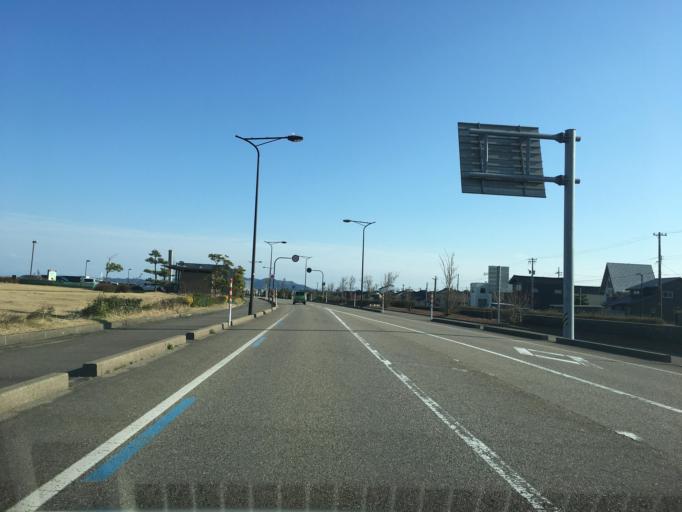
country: JP
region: Toyama
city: Himi
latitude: 36.8695
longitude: 136.9844
